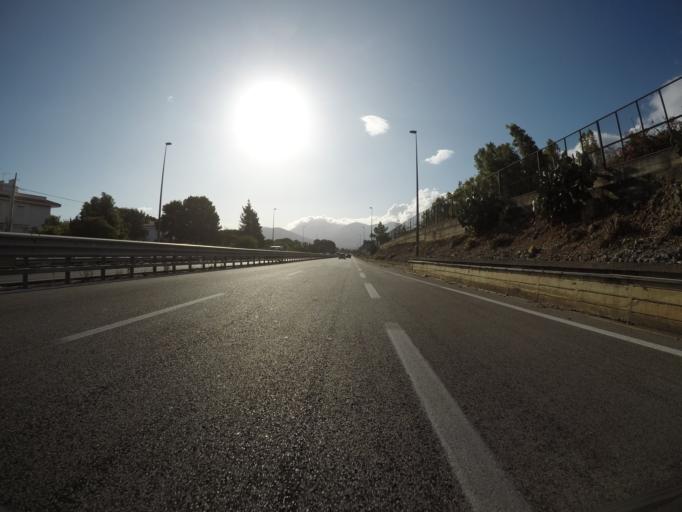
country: IT
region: Sicily
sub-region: Palermo
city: Carini
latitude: 38.1736
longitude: 13.1585
